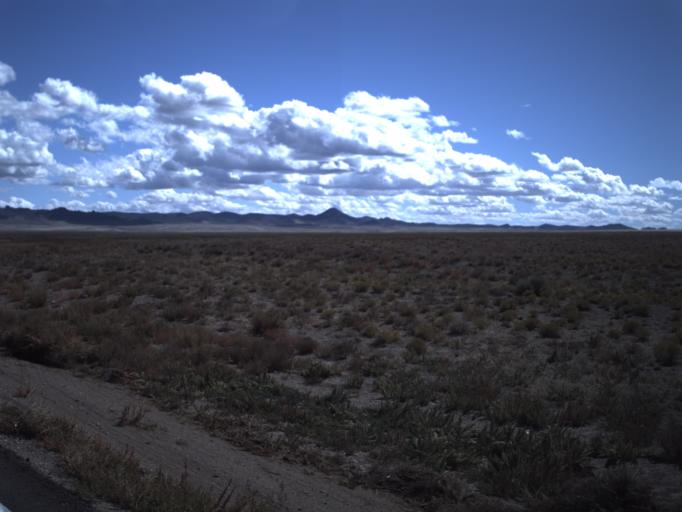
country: US
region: Utah
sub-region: Beaver County
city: Milford
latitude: 38.4770
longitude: -113.4272
